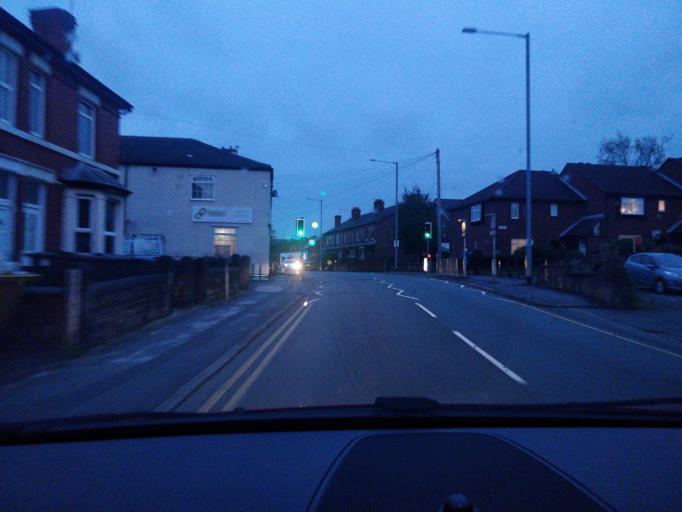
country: GB
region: England
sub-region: Lancashire
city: Ormskirk
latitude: 53.5667
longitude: -2.8799
